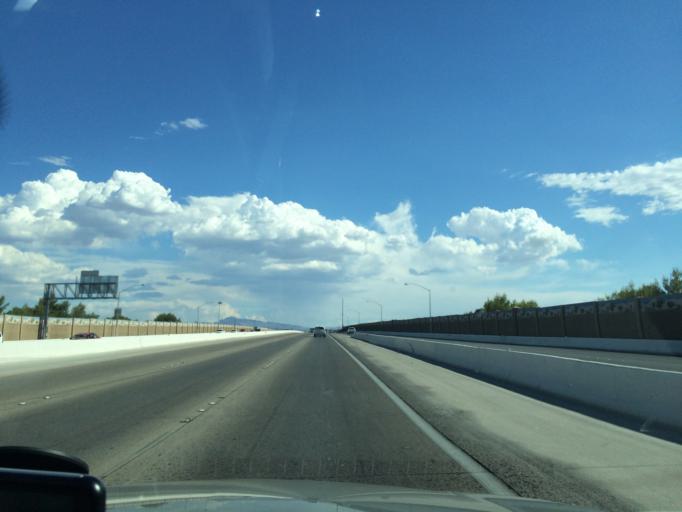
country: US
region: Nevada
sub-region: Clark County
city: Winchester
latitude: 36.1552
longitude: -115.0917
